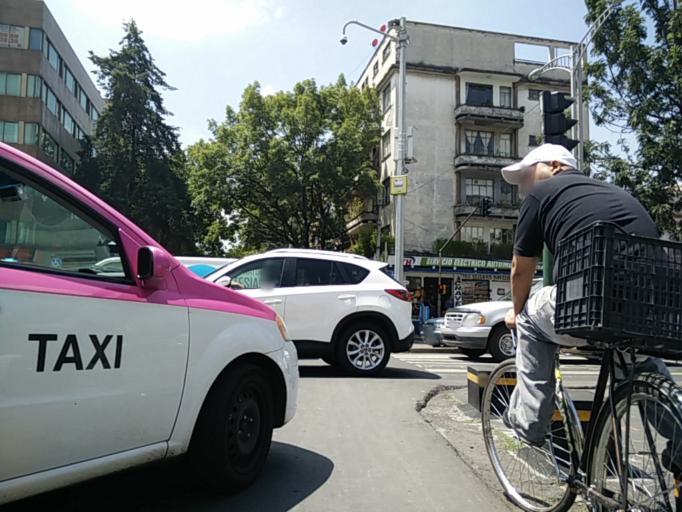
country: MX
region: Mexico City
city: Benito Juarez
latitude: 19.4228
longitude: -99.1672
